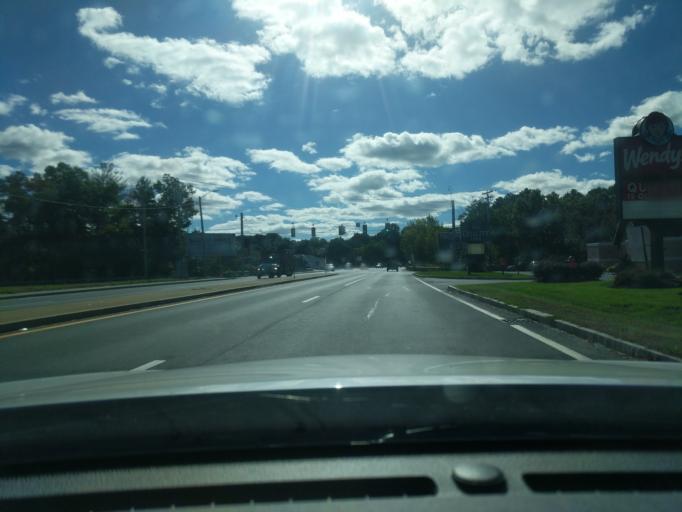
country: US
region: Massachusetts
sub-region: Hampden County
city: Westfield
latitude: 42.1415
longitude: -72.7334
